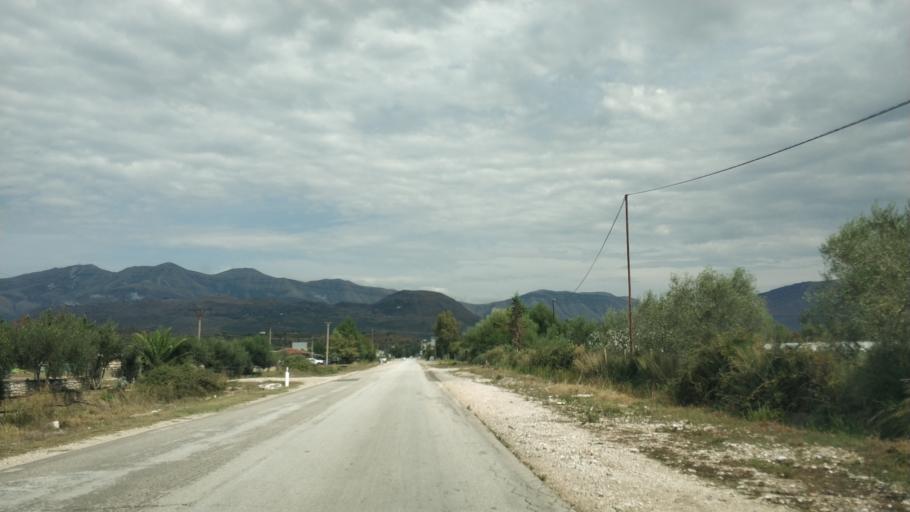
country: AL
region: Vlore
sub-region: Rrethi i Delvines
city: Finiq
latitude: 39.8926
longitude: 20.0675
